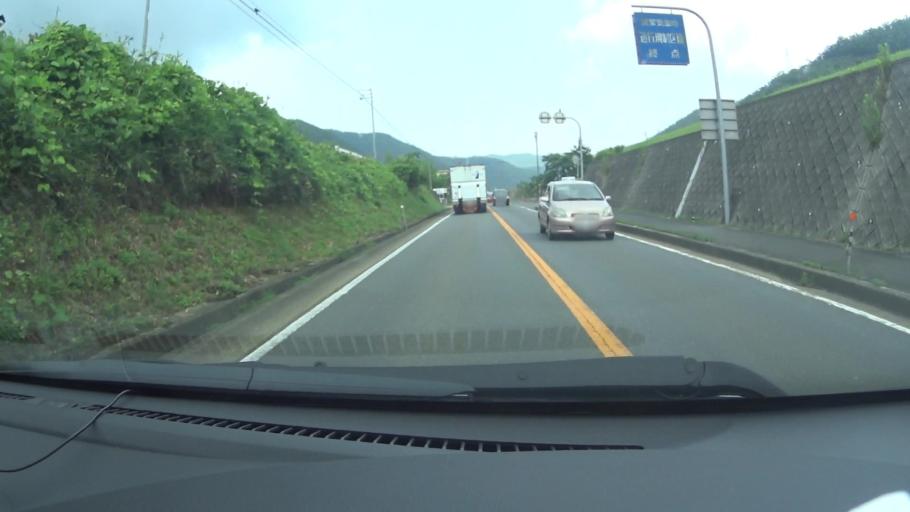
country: JP
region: Kyoto
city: Ayabe
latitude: 35.2232
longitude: 135.4190
